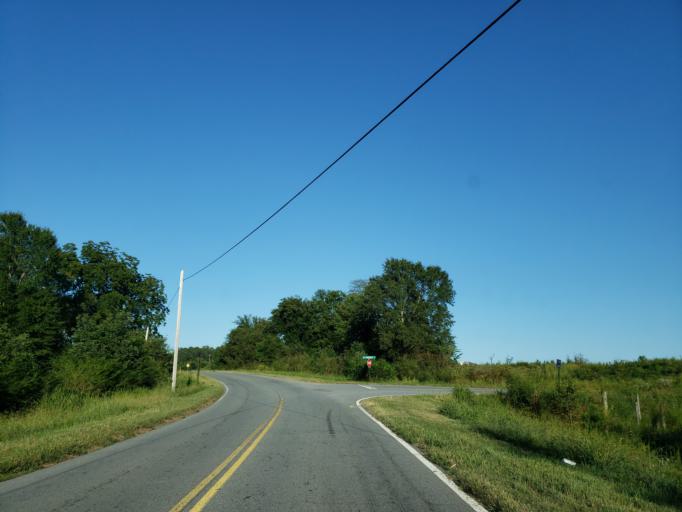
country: US
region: Georgia
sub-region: Bartow County
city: Rydal
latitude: 34.2720
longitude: -84.7922
